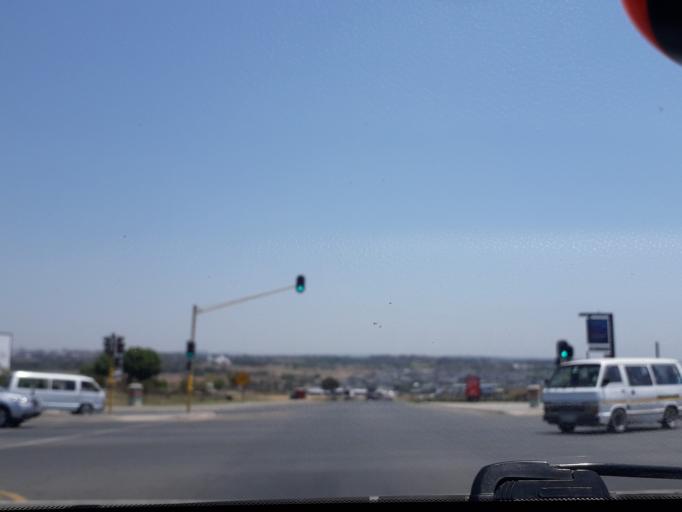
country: ZA
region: Gauteng
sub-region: City of Johannesburg Metropolitan Municipality
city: Midrand
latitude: -26.0231
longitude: 28.1179
